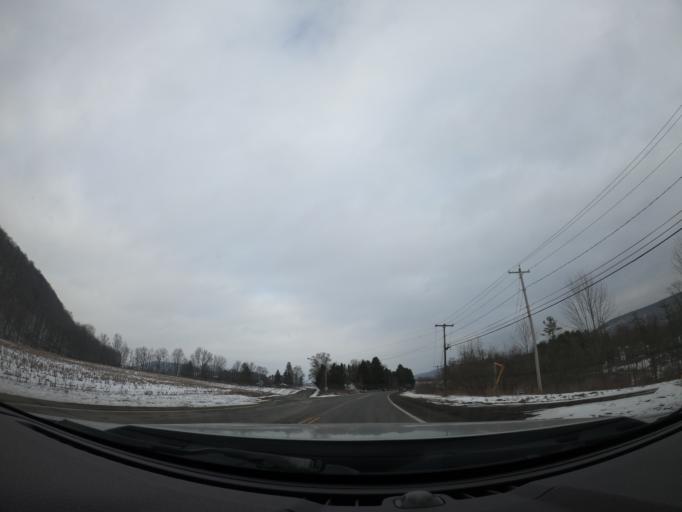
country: US
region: New York
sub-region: Cortland County
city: Homer
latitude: 42.7157
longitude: -76.1543
